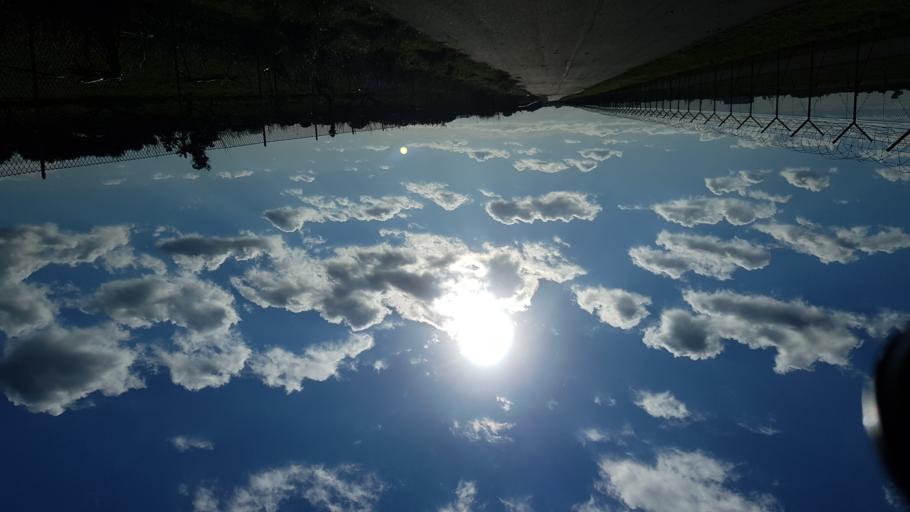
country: IT
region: Apulia
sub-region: Provincia di Brindisi
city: Materdomini
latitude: 40.6671
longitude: 17.9333
